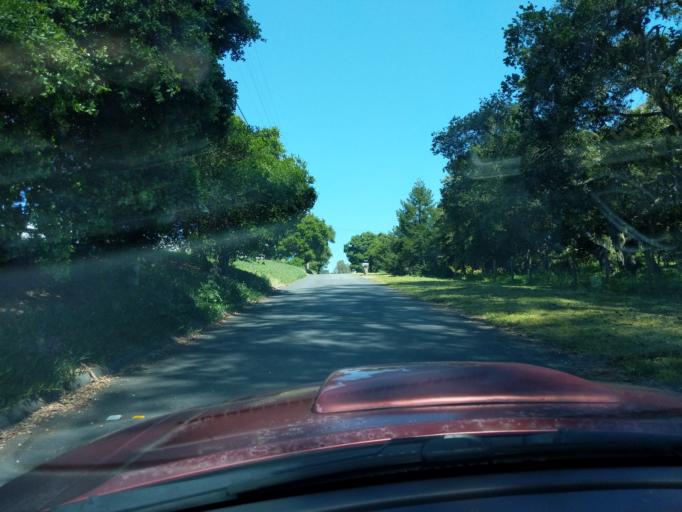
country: US
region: California
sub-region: Monterey County
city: Las Lomas
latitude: 36.8704
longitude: -121.6874
